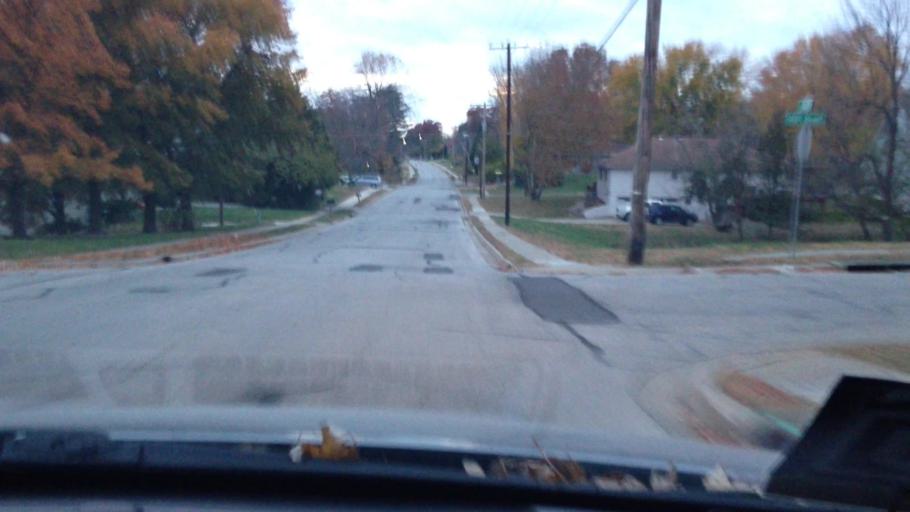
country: US
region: Kansas
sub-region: Leavenworth County
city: Leavenworth
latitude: 39.2906
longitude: -94.9416
